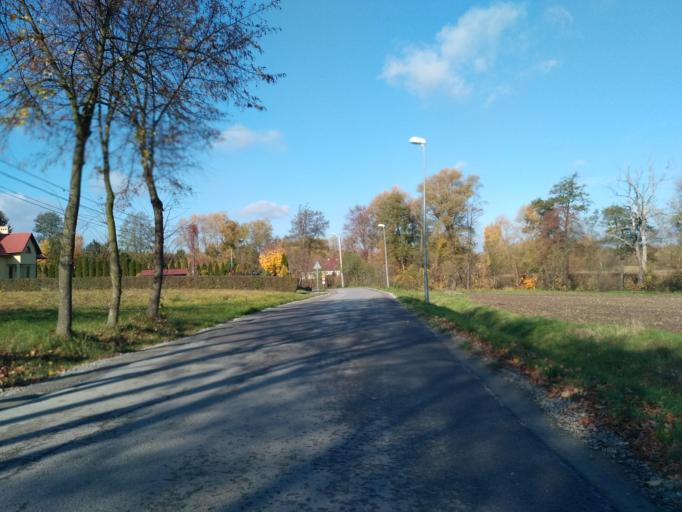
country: PL
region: Subcarpathian Voivodeship
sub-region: Powiat rzeszowski
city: Niechobrz
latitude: 50.0091
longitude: 21.8978
